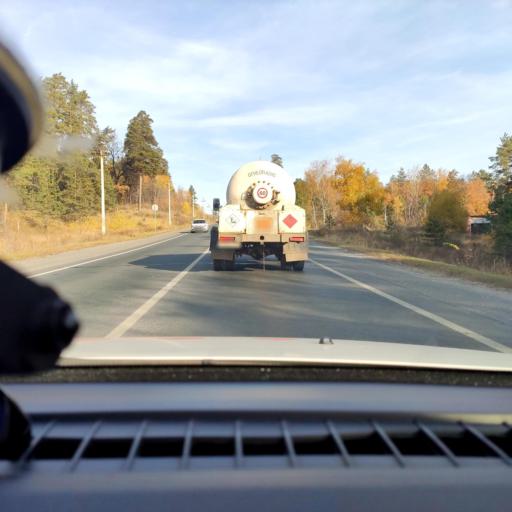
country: RU
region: Samara
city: Volzhskiy
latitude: 53.4430
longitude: 50.1234
